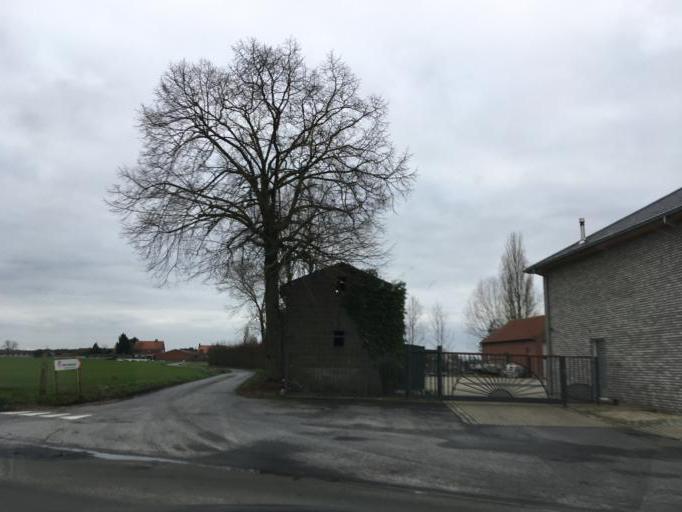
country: BE
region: Flanders
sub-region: Provincie West-Vlaanderen
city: Roeselare
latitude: 50.9024
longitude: 3.1296
